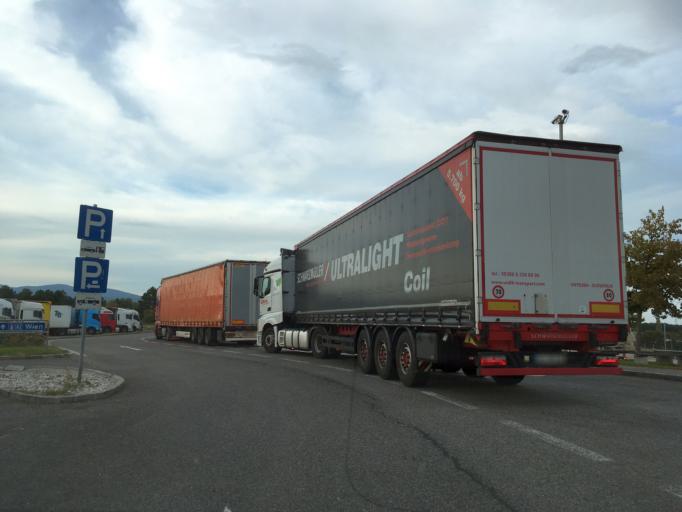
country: AT
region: Lower Austria
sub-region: Politischer Bezirk Baden
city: Leobersdorf
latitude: 47.9097
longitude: 16.2090
